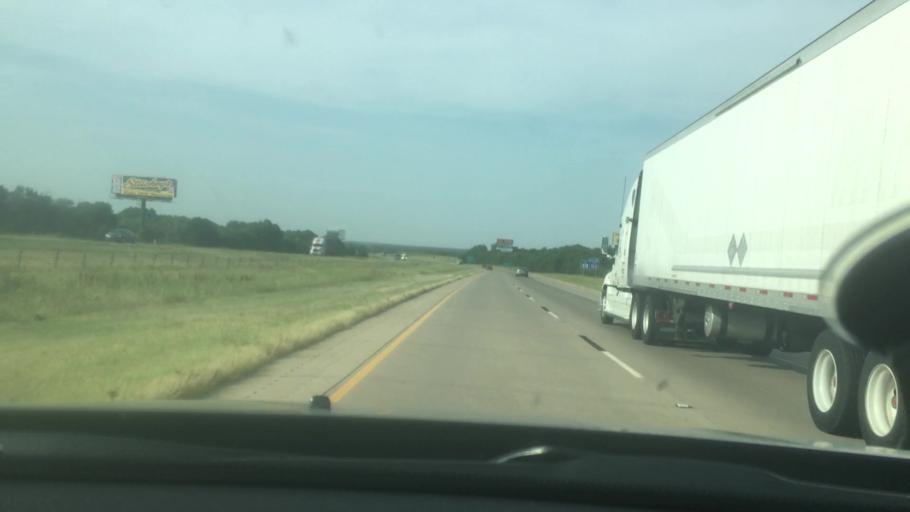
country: US
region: Oklahoma
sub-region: Carter County
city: Ardmore
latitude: 34.3136
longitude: -97.1578
